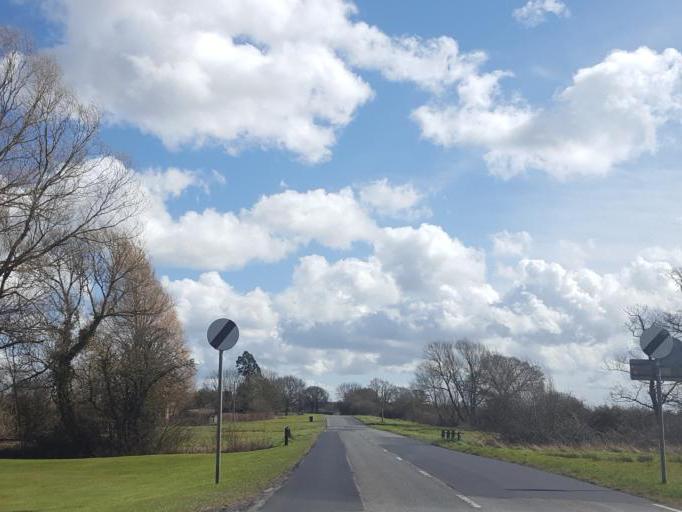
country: GB
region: England
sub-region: Worcestershire
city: Kempsey
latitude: 52.1062
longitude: -2.2644
